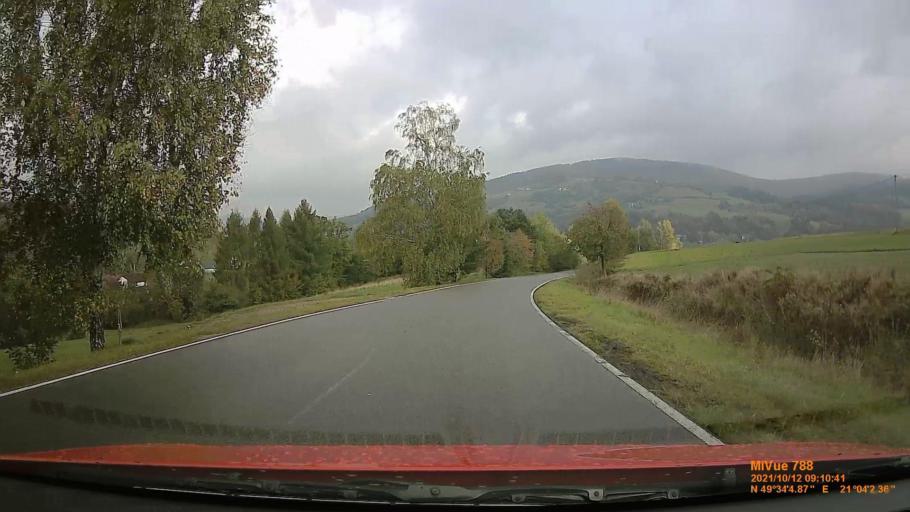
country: PL
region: Lesser Poland Voivodeship
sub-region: Powiat gorlicki
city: Ropa
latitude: 49.5682
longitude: 21.0673
